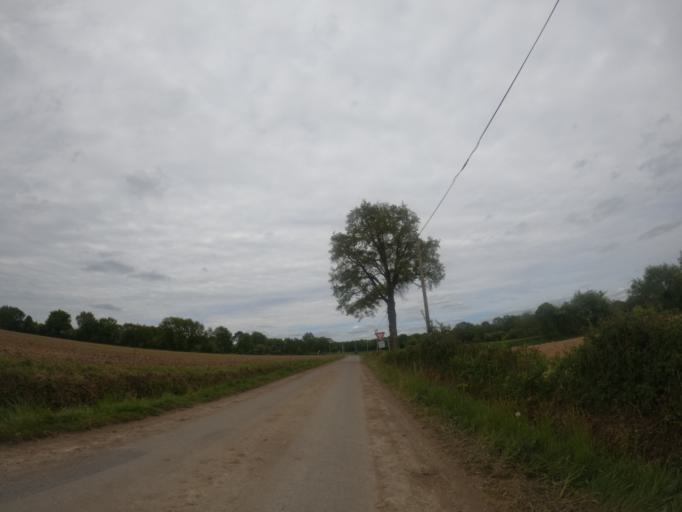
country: FR
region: Pays de la Loire
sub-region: Departement de la Loire-Atlantique
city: Rouge
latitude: 47.7372
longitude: -1.4432
